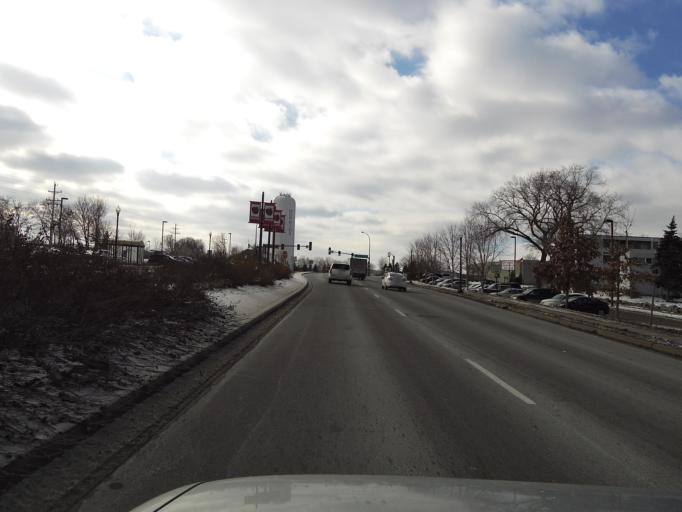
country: US
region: Minnesota
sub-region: Hennepin County
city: Minnetonka Mills
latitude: 44.9216
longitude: -93.4087
